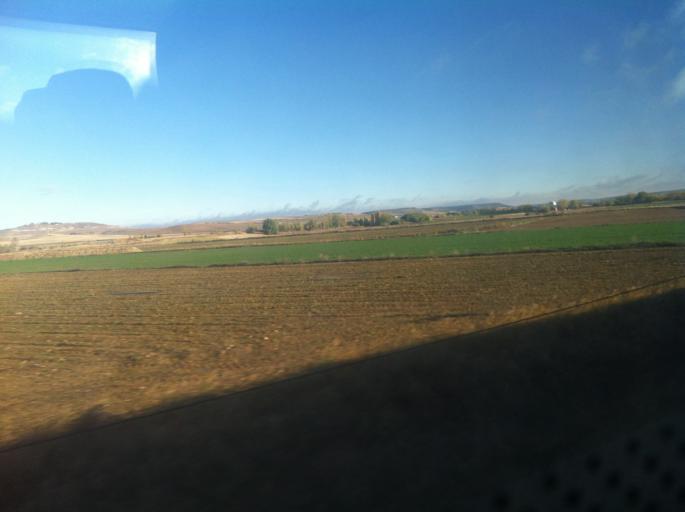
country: ES
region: Castille and Leon
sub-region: Provincia de Palencia
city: Torquemada
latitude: 42.0088
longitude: -4.3411
